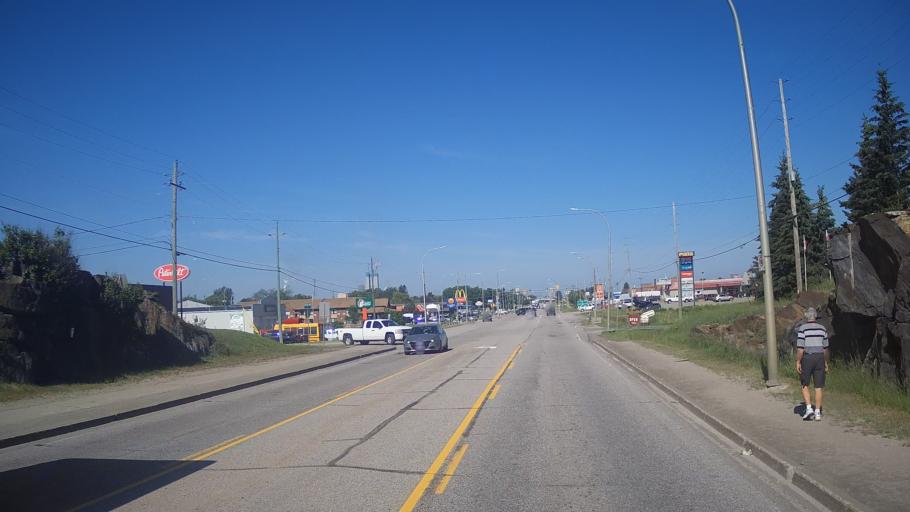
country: CA
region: Ontario
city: Dryden
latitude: 49.7862
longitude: -92.8185
